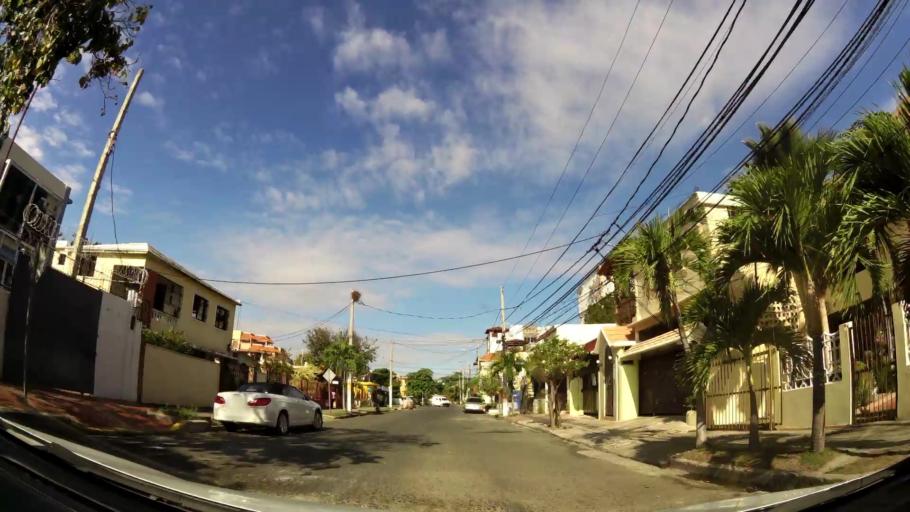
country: DO
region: Santo Domingo
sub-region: Santo Domingo
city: Santo Domingo Este
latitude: 18.4872
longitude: -69.8671
